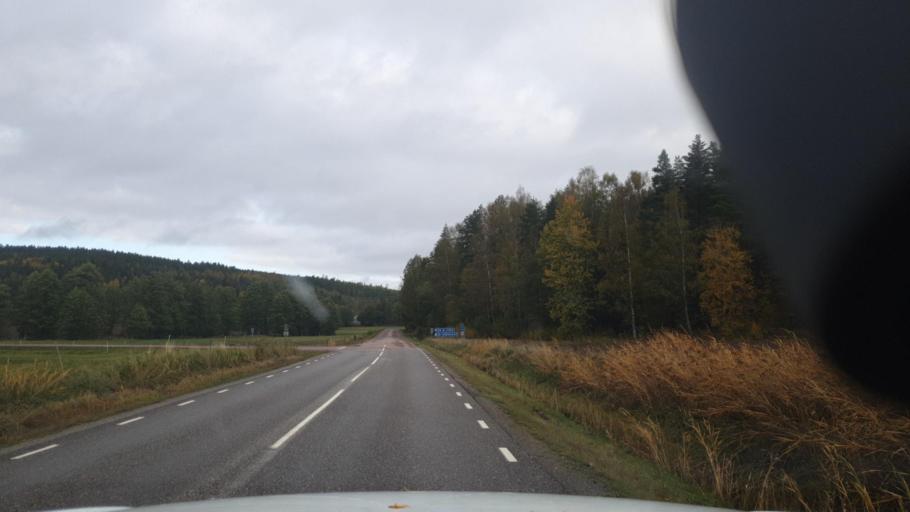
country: SE
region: Vaermland
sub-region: Grums Kommun
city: Grums
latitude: 59.3992
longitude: 13.0705
